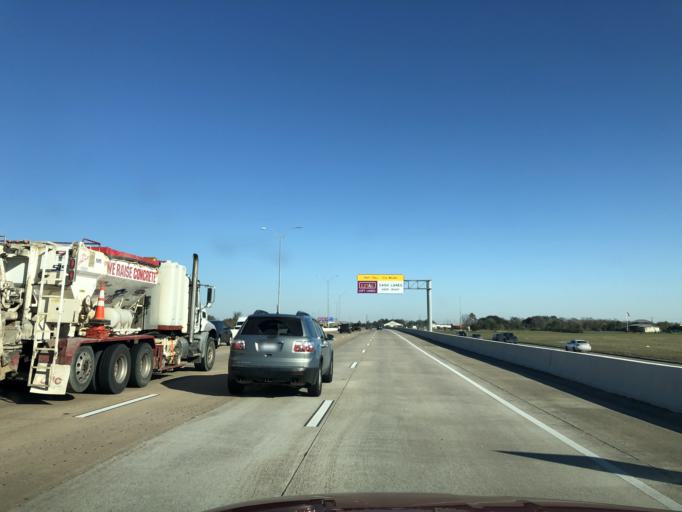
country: US
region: Texas
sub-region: Fort Bend County
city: Fresno
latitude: 29.5963
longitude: -95.4371
